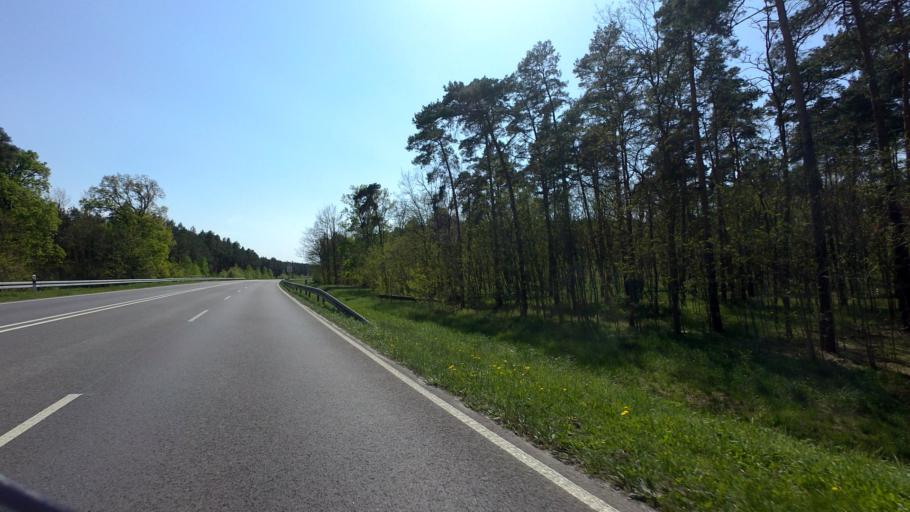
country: DE
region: Brandenburg
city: Beeskow
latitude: 52.1558
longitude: 14.2167
